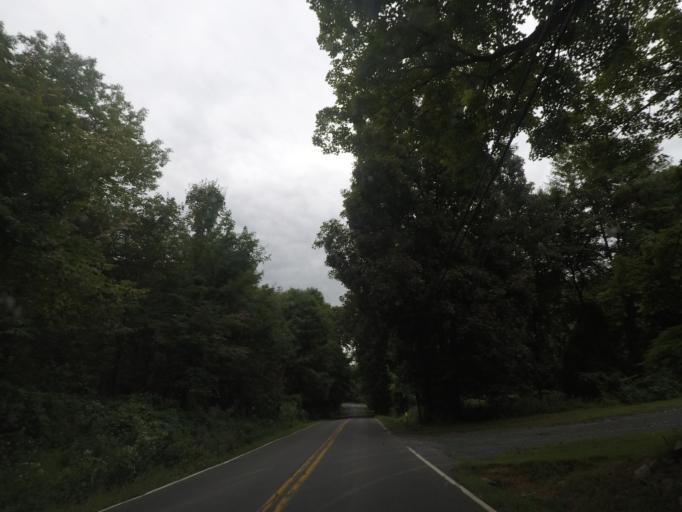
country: US
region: New York
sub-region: Rensselaer County
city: Nassau
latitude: 42.4774
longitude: -73.5917
